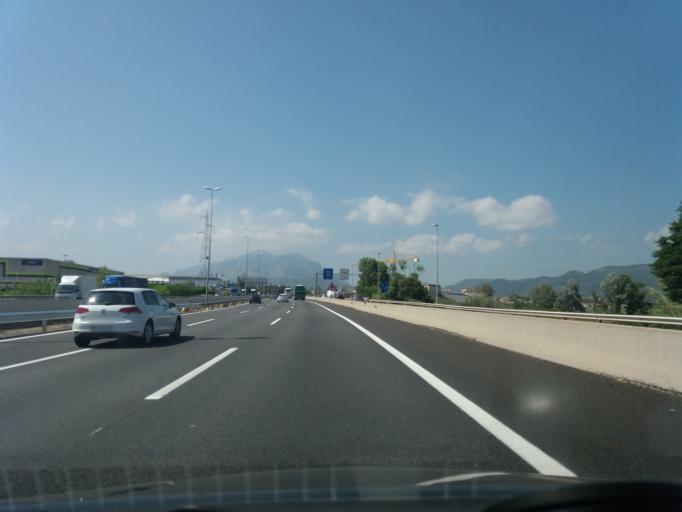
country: ES
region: Catalonia
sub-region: Provincia de Barcelona
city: Abrera
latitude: 41.5070
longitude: 1.9047
